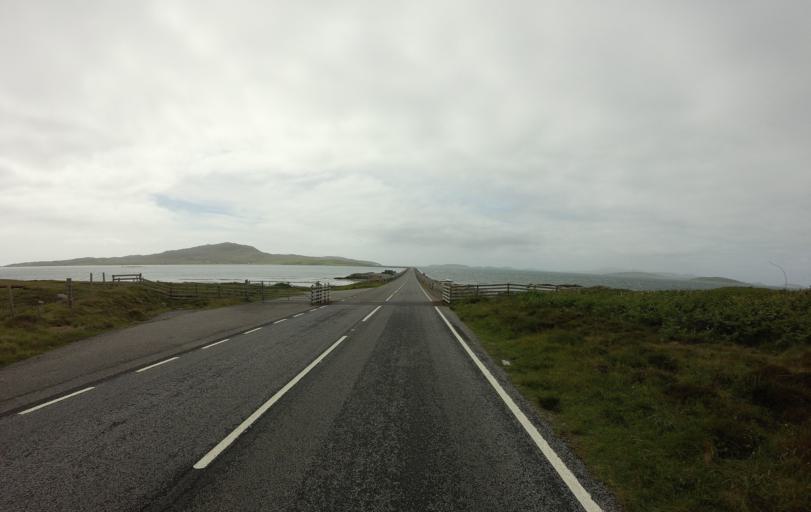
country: GB
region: Scotland
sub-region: Eilean Siar
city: Isle of South Uist
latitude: 57.1036
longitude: -7.3178
